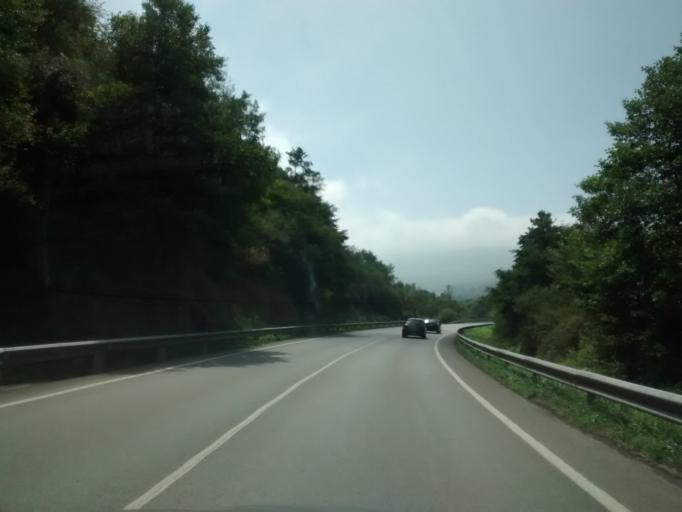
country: ES
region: Cantabria
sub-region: Provincia de Cantabria
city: Ruente
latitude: 43.2731
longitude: -4.2455
